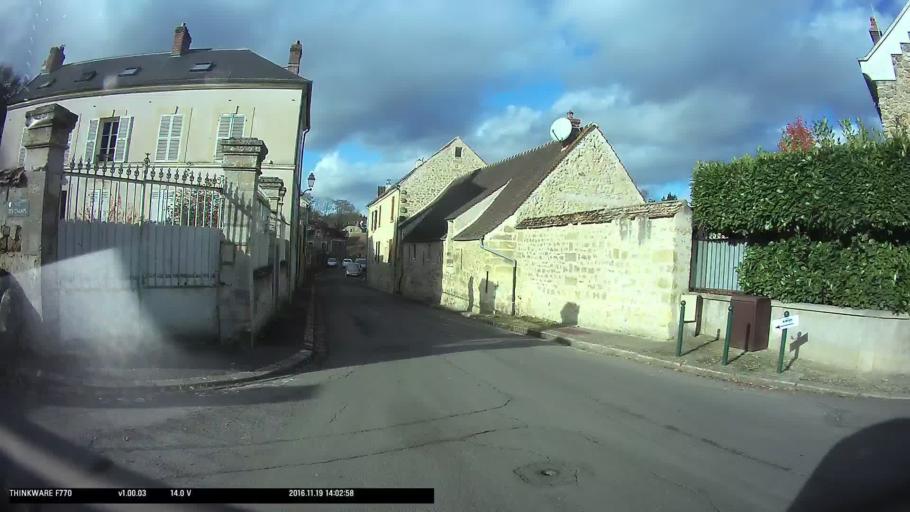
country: FR
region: Ile-de-France
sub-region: Departement du Val-d'Oise
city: Ableiges
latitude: 49.0756
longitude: 2.0049
